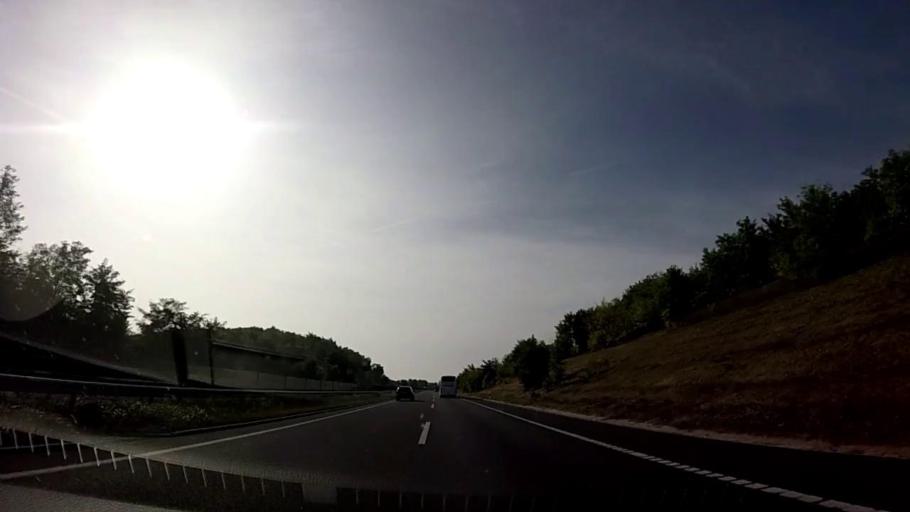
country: HU
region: Somogy
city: Zamardi
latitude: 46.8442
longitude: 17.9532
